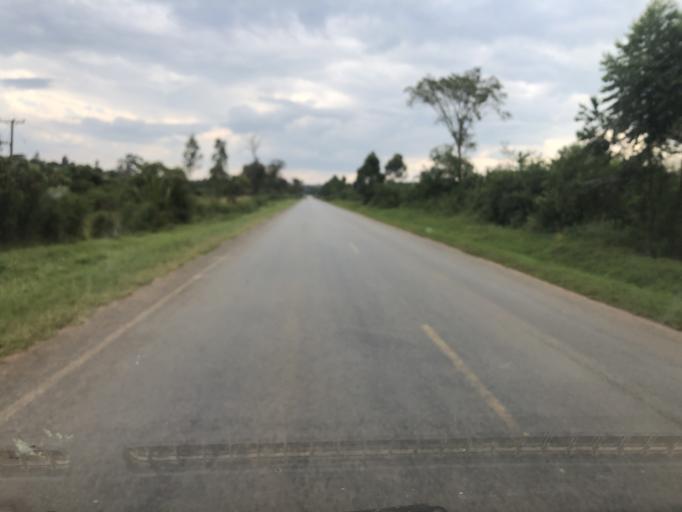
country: UG
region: Western Region
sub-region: Sheema District
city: Kibingo
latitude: -0.5800
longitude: 30.4311
